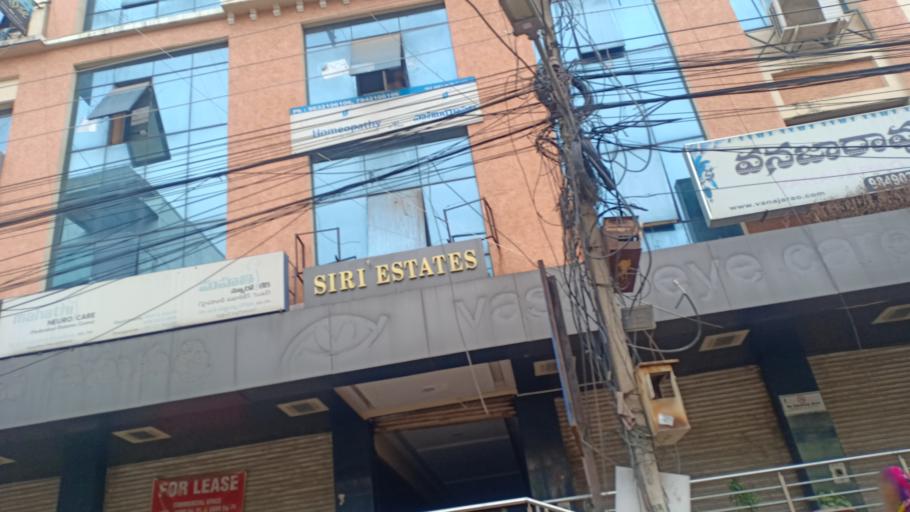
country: IN
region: Telangana
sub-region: Hyderabad
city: Hyderabad
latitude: 17.4320
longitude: 78.4454
